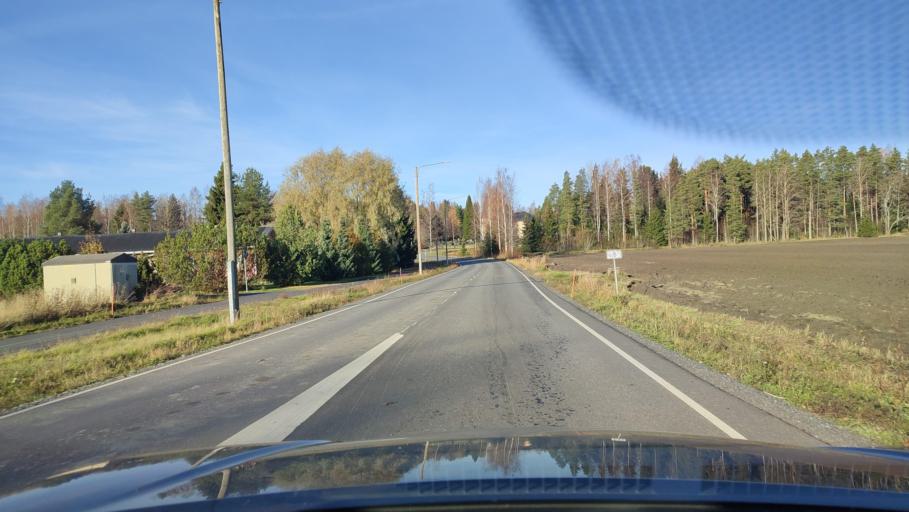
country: FI
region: Southern Ostrobothnia
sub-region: Suupohja
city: Karijoki
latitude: 62.3098
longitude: 21.7099
